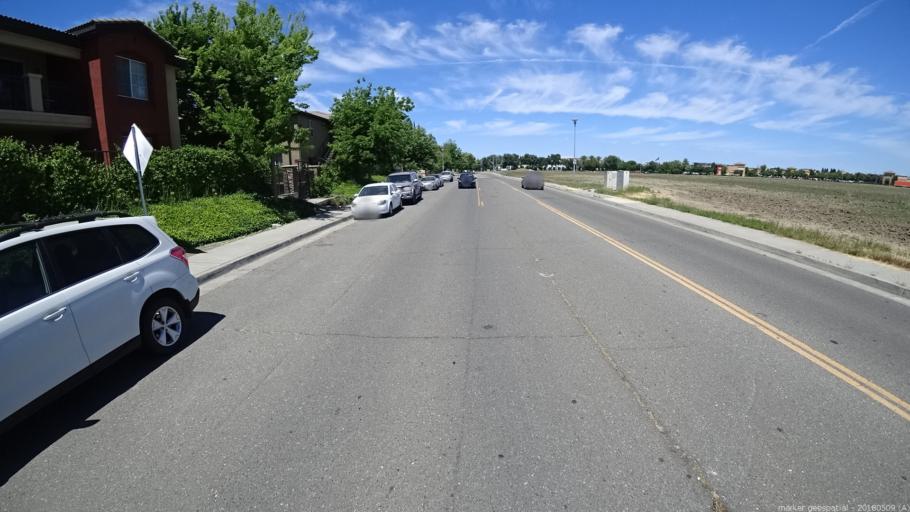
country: US
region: California
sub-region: Sacramento County
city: Sacramento
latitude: 38.6441
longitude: -121.5118
